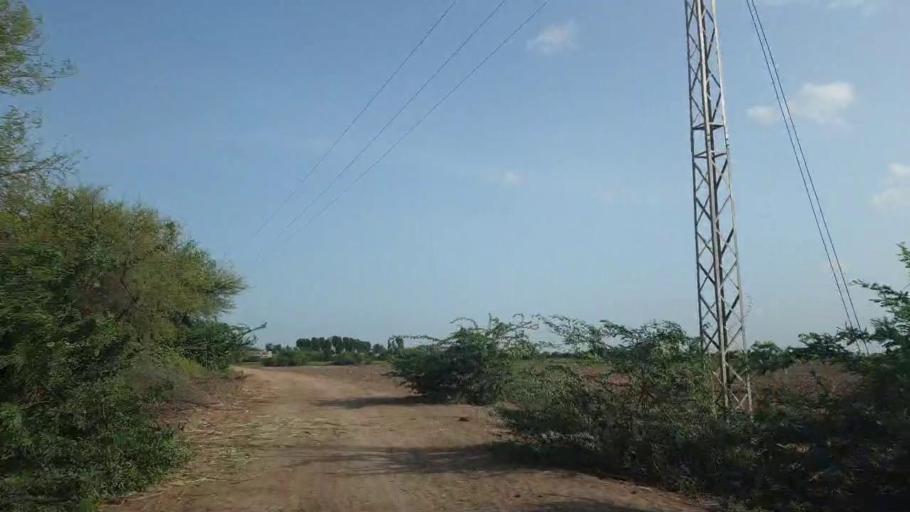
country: PK
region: Sindh
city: Kadhan
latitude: 24.6258
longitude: 69.0845
